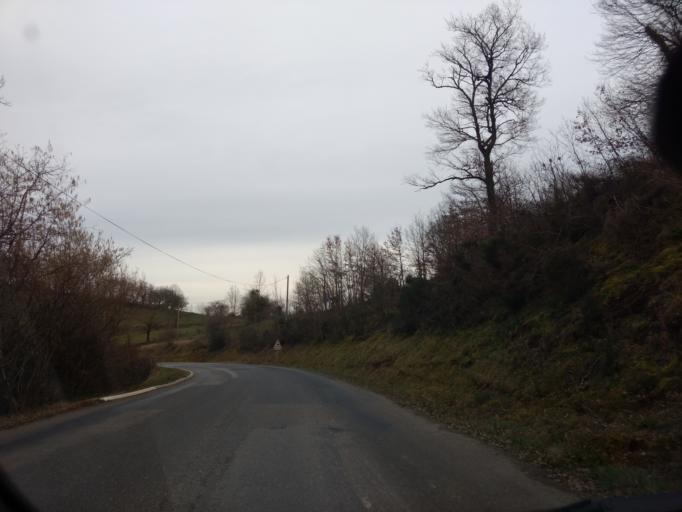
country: FR
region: Midi-Pyrenees
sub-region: Departement de l'Aveyron
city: Saint-Christophe-Vallon
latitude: 44.4569
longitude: 2.4015
